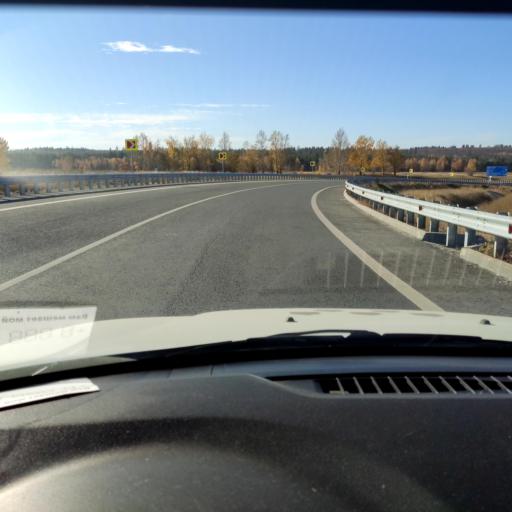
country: RU
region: Samara
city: Bereza
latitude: 53.4907
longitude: 50.1152
